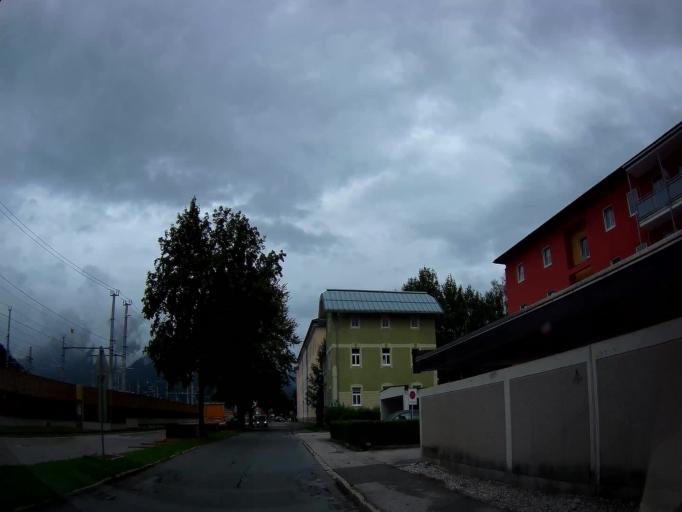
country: AT
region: Salzburg
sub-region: Politischer Bezirk Zell am See
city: Saalfelden am Steinernen Meer
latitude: 47.4247
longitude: 12.8309
